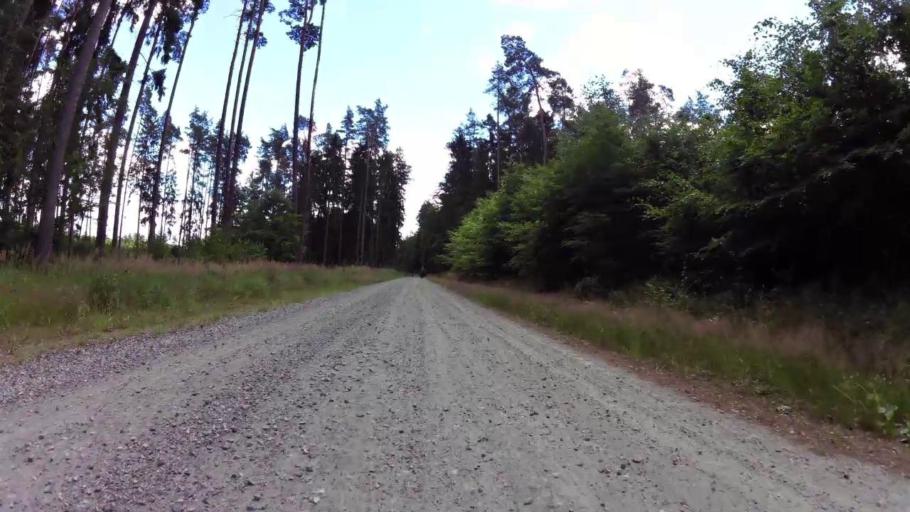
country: PL
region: West Pomeranian Voivodeship
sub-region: Powiat lobeski
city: Radowo Male
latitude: 53.7235
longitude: 15.5348
